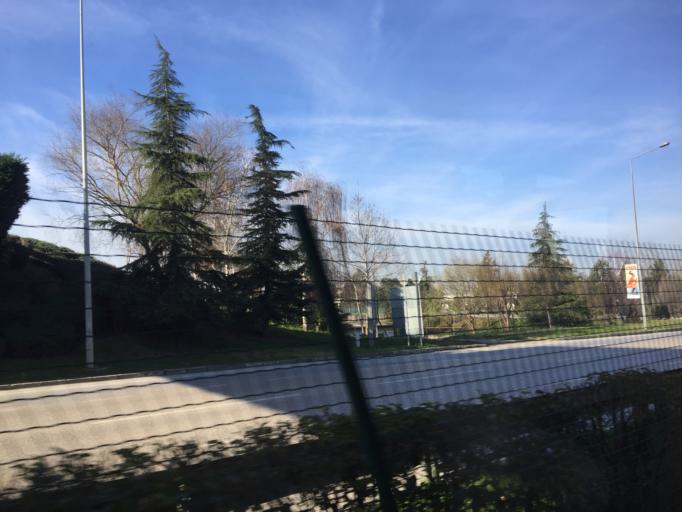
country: TR
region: Bursa
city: Niluefer
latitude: 40.2390
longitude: 28.9728
